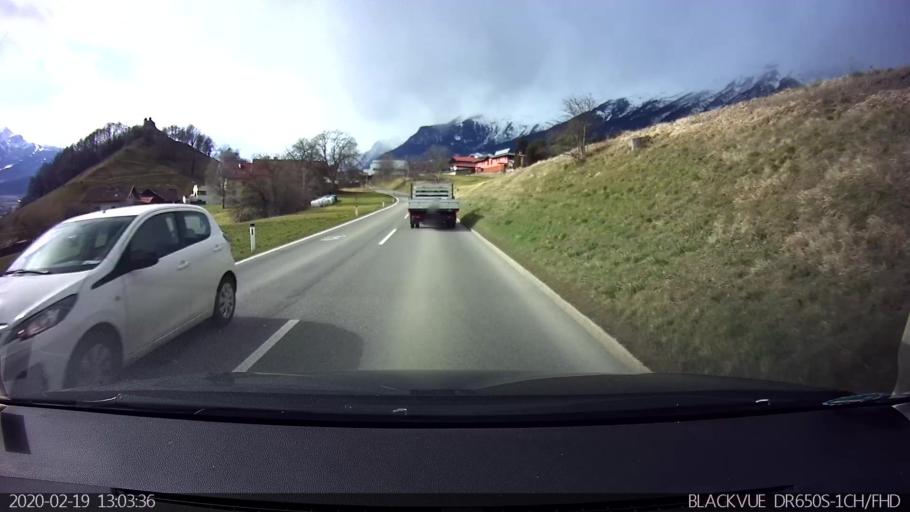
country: AT
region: Tyrol
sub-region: Politischer Bezirk Innsbruck Land
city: Rum
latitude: 47.2849
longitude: 11.4388
